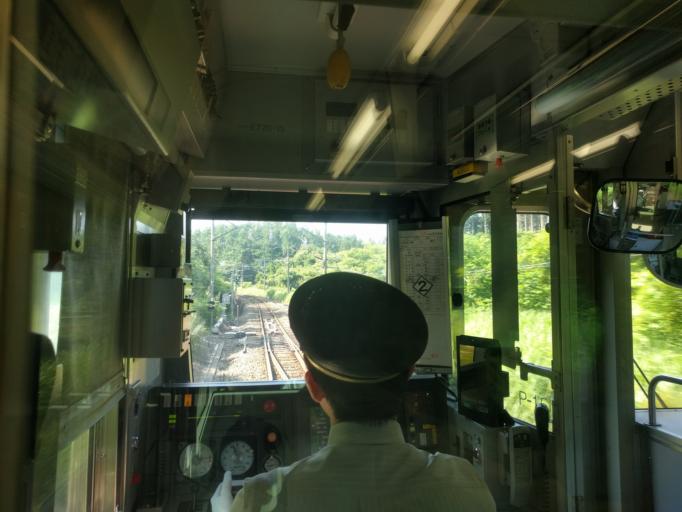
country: JP
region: Fukushima
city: Inawashiro
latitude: 37.5479
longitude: 140.0176
